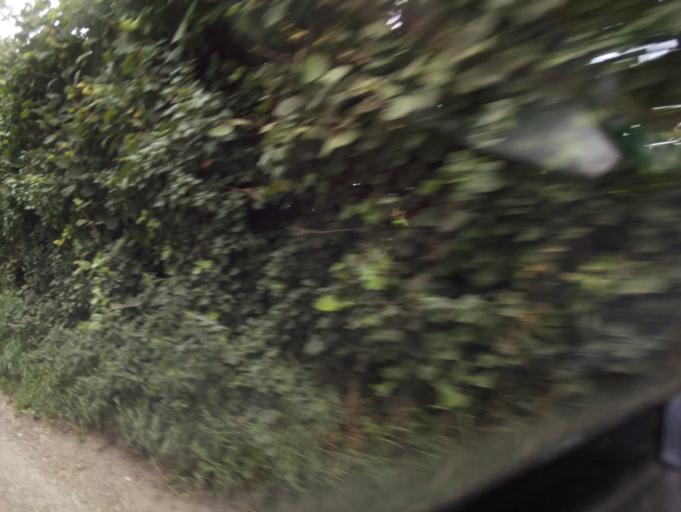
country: GB
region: England
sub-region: Somerset
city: Bradley Cross
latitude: 51.2623
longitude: -2.7597
